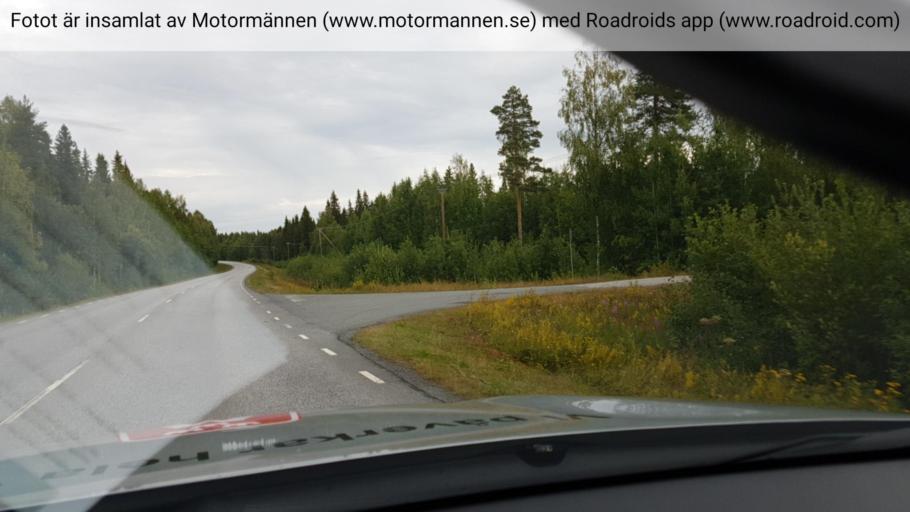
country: SE
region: Norrbotten
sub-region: Bodens Kommun
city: Boden
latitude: 65.8014
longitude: 21.6578
